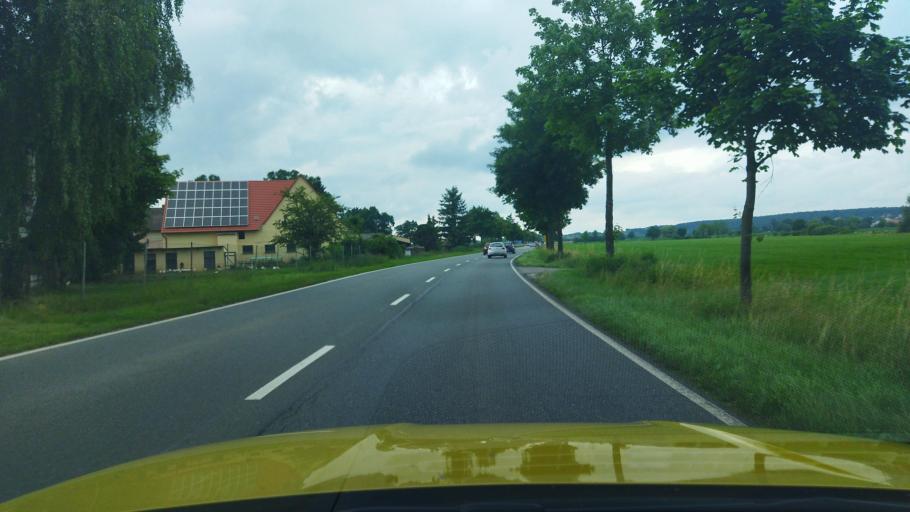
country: DE
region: Bavaria
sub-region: Regierungsbezirk Mittelfranken
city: Gunzenhausen
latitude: 49.1299
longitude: 10.7450
